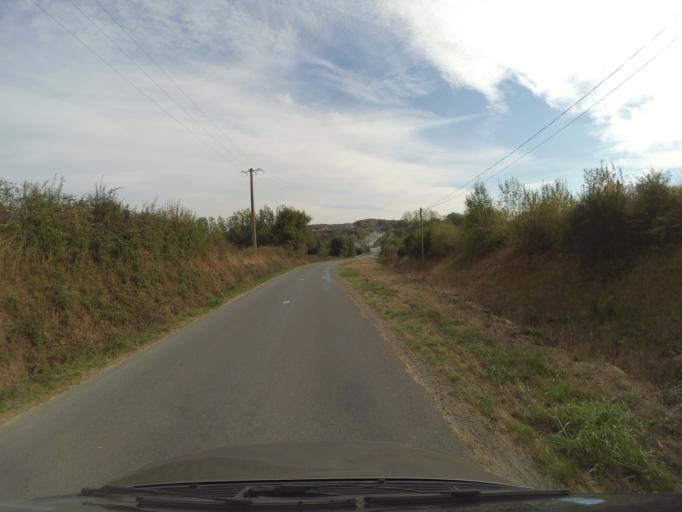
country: FR
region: Pays de la Loire
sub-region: Departement de Maine-et-Loire
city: Villedieu-la-Blouere
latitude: 47.1545
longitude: -1.0472
